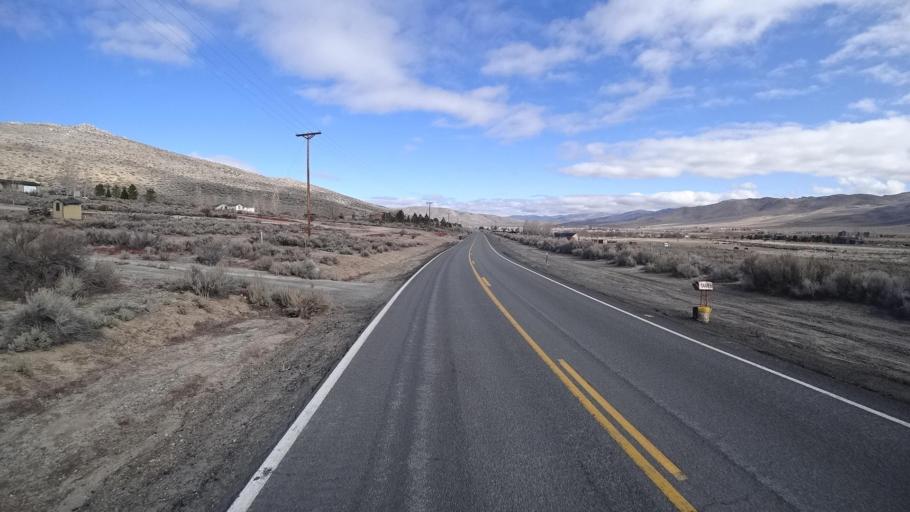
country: US
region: Nevada
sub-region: Washoe County
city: Cold Springs
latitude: 39.8464
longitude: -119.9355
